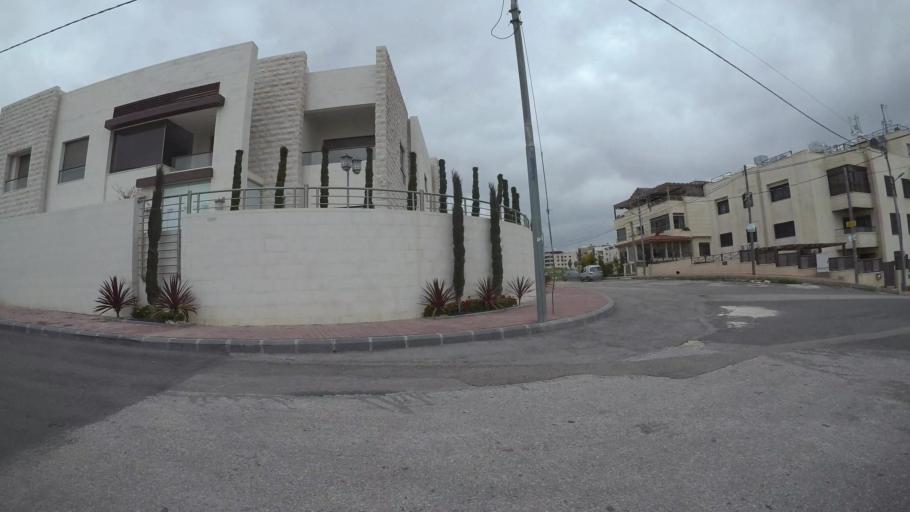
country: JO
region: Amman
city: Wadi as Sir
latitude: 31.9914
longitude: 35.8360
